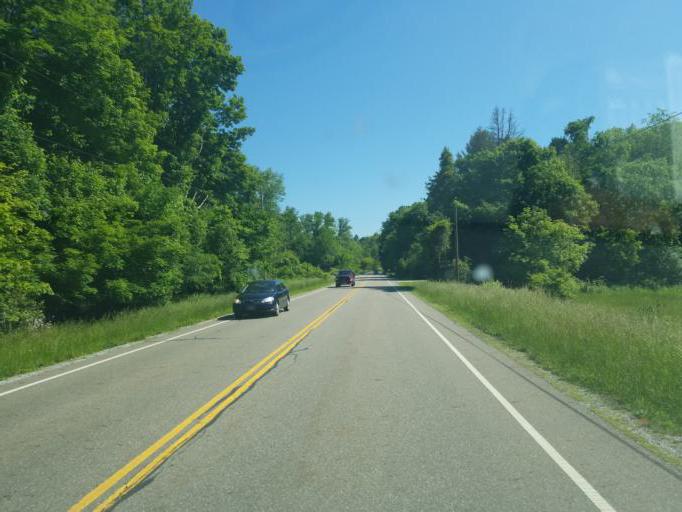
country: US
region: Ohio
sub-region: Summit County
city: Peninsula
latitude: 41.2062
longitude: -81.5619
